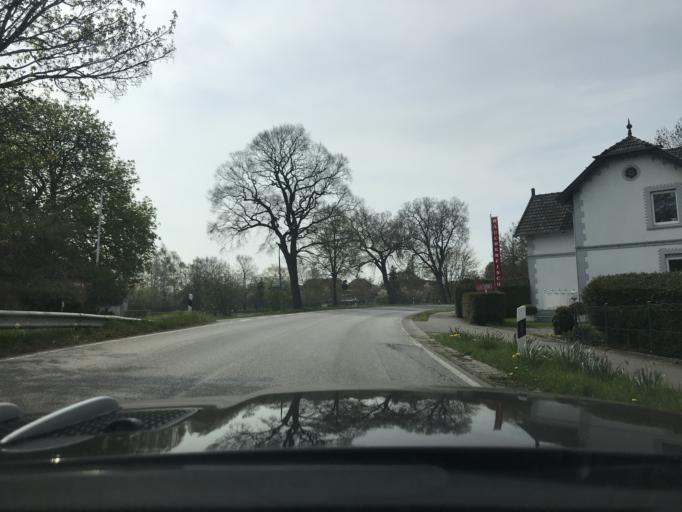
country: DE
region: Schleswig-Holstein
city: Grube
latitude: 54.2379
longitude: 11.0351
